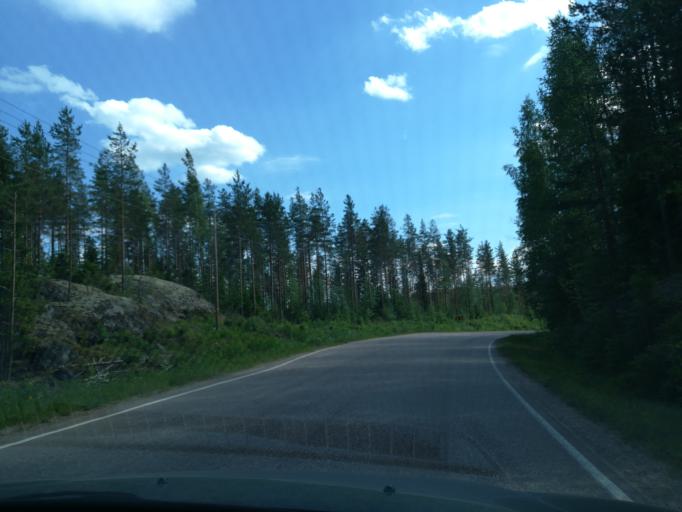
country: FI
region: South Karelia
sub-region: Imatra
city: Ruokolahti
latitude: 61.4802
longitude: 28.7888
